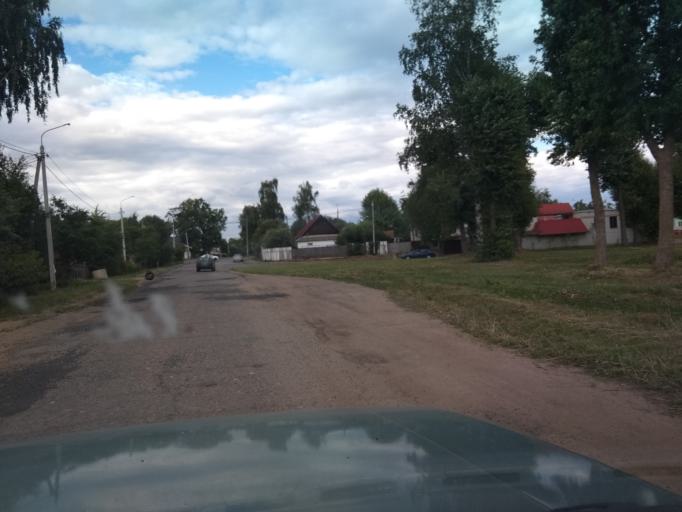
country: BY
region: Mogilev
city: Mahilyow
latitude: 53.9265
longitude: 30.3466
